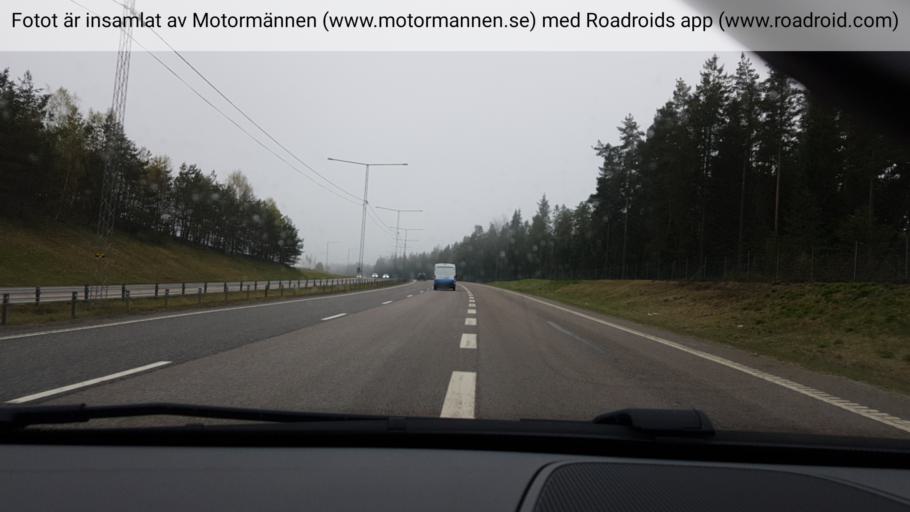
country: SE
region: Stockholm
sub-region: Haninge Kommun
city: Haninge
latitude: 59.1534
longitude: 18.1551
